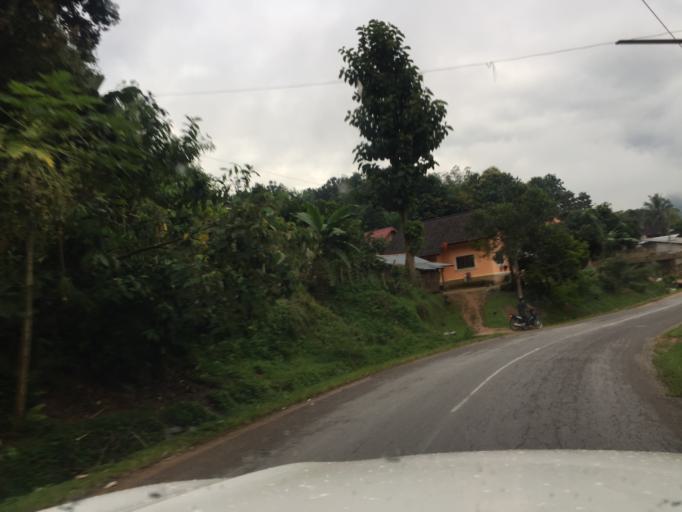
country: LA
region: Oudomxai
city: Muang La
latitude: 20.8659
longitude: 102.1216
